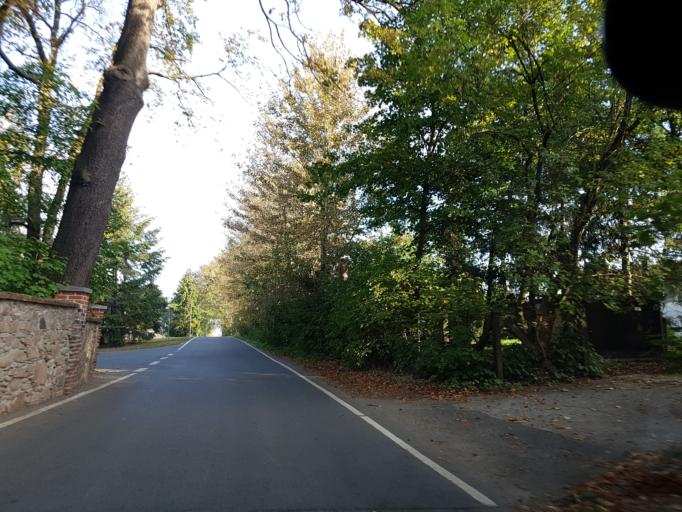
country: DE
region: Saxony
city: Dobeln
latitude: 51.1161
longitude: 13.0768
